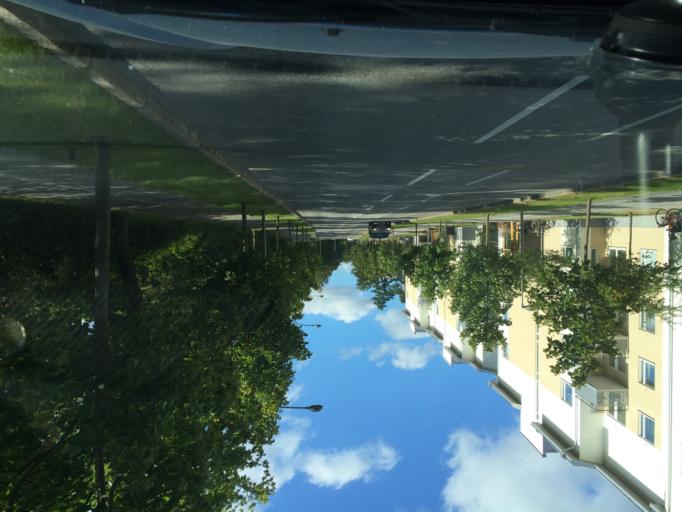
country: SE
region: Stockholm
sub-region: Nacka Kommun
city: Nacka
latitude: 59.2807
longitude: 18.1198
